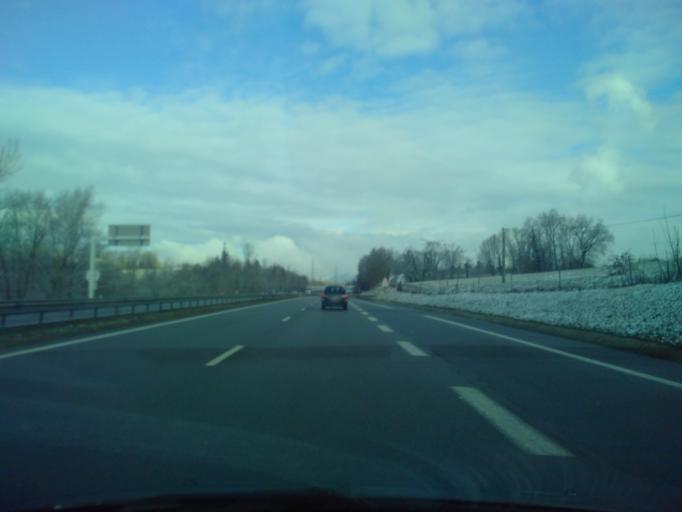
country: FR
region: Rhone-Alpes
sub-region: Departement de la Haute-Savoie
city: Chavanod
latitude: 45.8514
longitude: 6.0567
